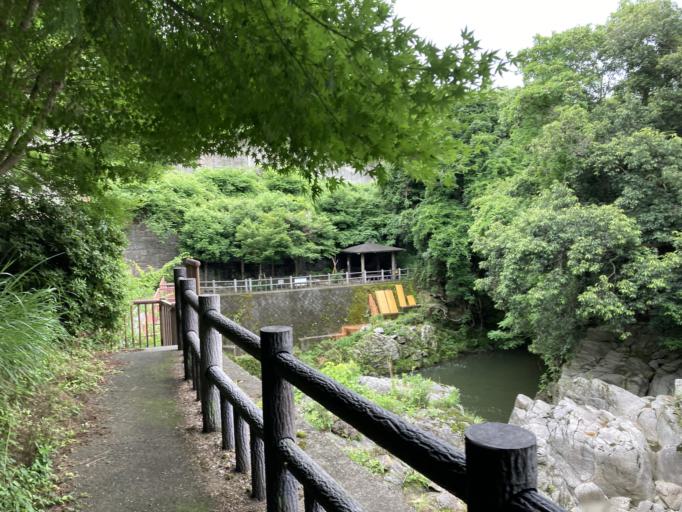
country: JP
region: Nara
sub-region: Ikoma-shi
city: Ikoma
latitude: 34.6463
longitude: 135.7069
